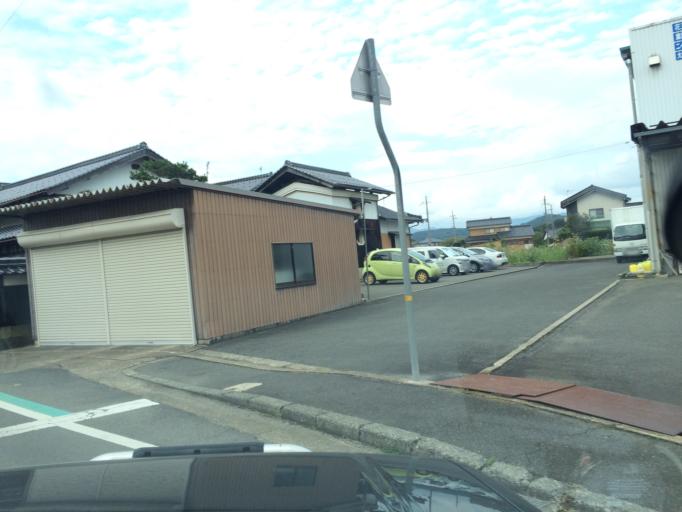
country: JP
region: Hyogo
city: Toyooka
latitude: 35.4928
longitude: 134.8028
